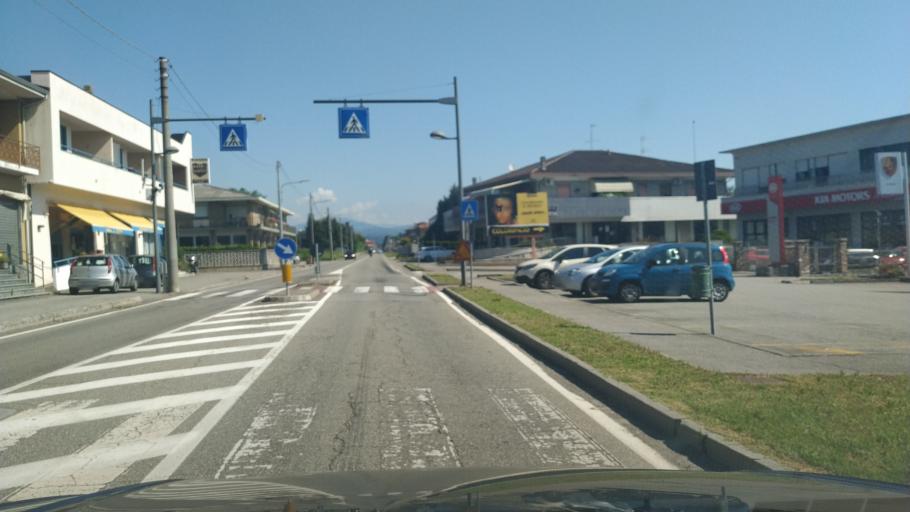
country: IT
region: Piedmont
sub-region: Provincia di Novara
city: Cureggio
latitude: 45.6778
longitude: 8.4562
